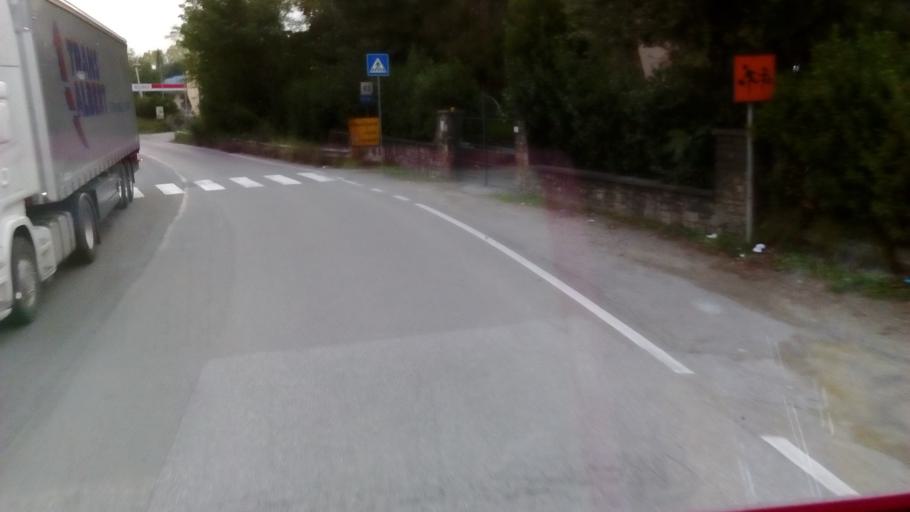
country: IT
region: Tuscany
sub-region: Province of Florence
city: Castelfiorentino
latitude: 43.6188
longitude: 10.9640
